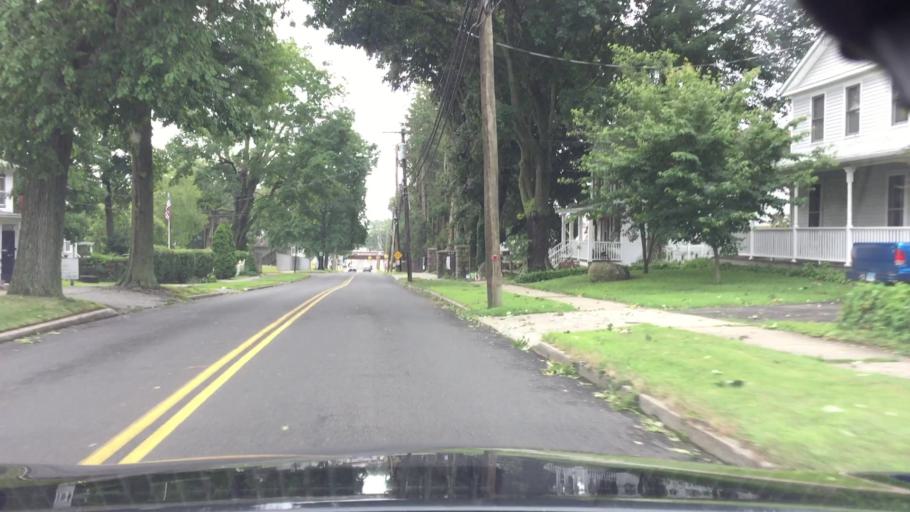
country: US
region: Connecticut
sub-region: New Haven County
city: City of Milford (balance)
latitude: 41.2246
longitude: -73.0623
